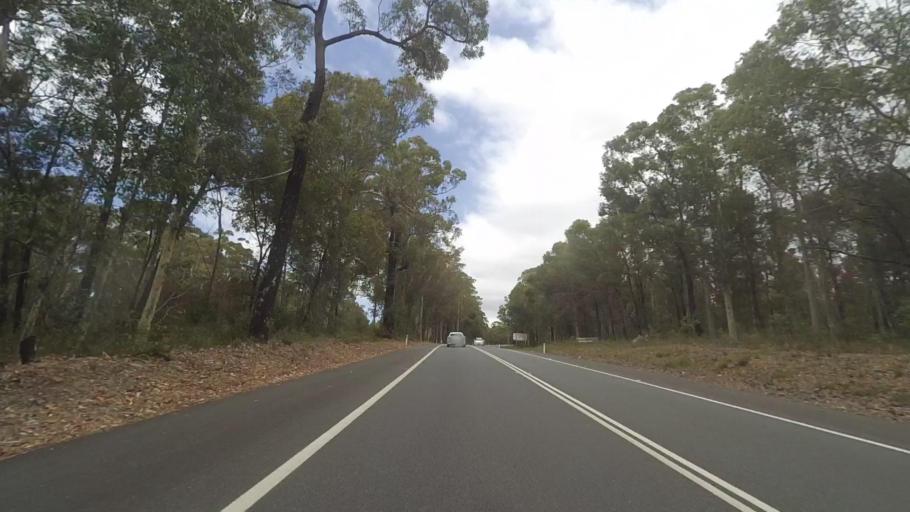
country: AU
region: New South Wales
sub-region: Shoalhaven Shire
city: Milton
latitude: -35.1439
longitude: 150.4627
